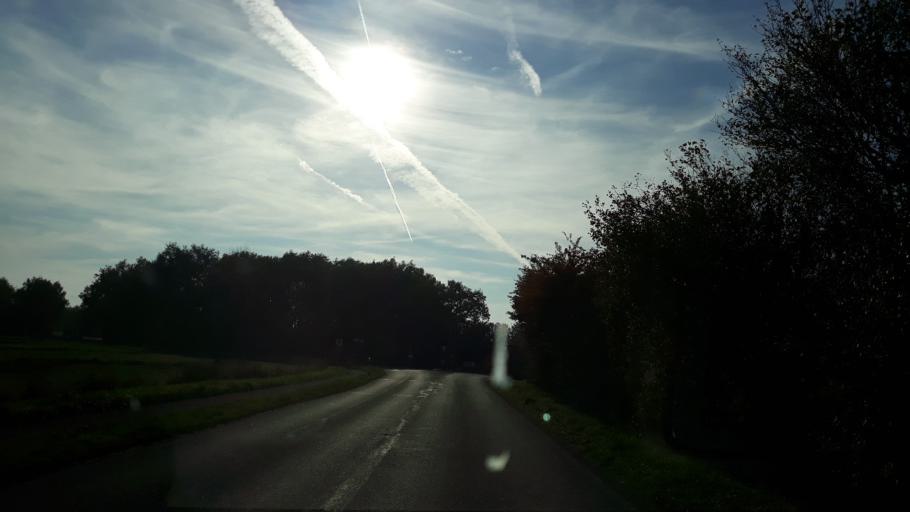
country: DE
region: Schleswig-Holstein
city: Borm
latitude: 54.4107
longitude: 9.3808
